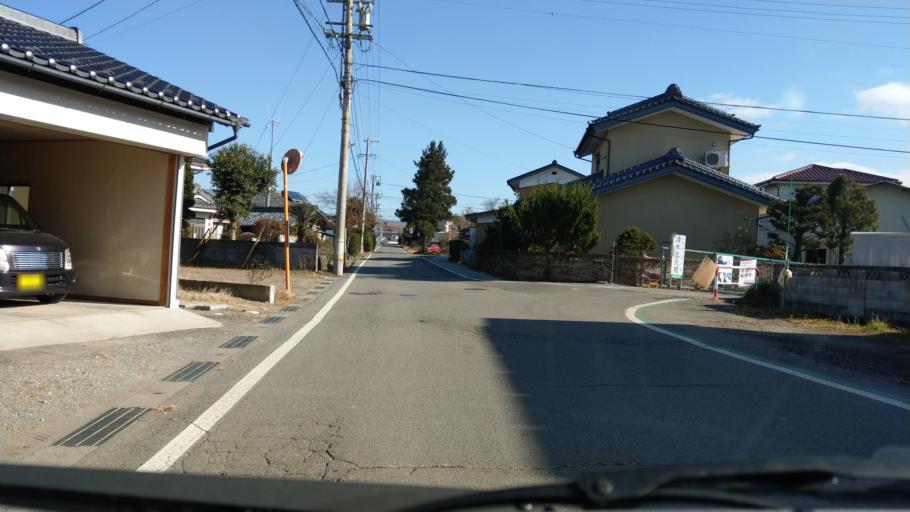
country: JP
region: Nagano
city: Komoro
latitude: 36.3036
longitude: 138.4761
